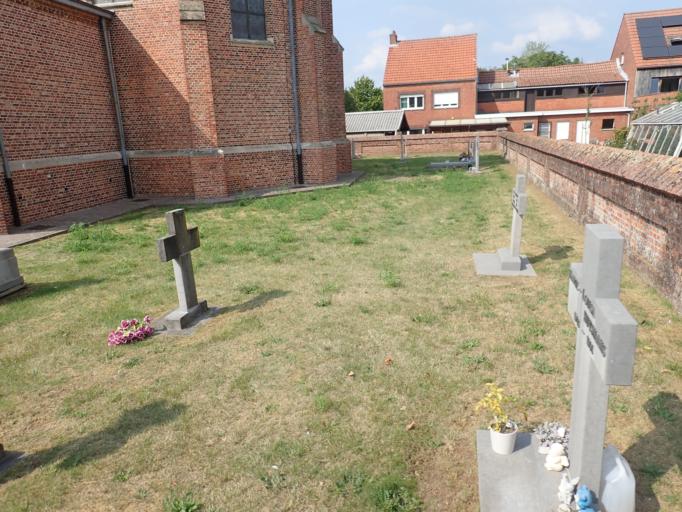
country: BE
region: Flanders
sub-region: Provincie Antwerpen
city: Meerhout
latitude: 51.1625
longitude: 5.0642
